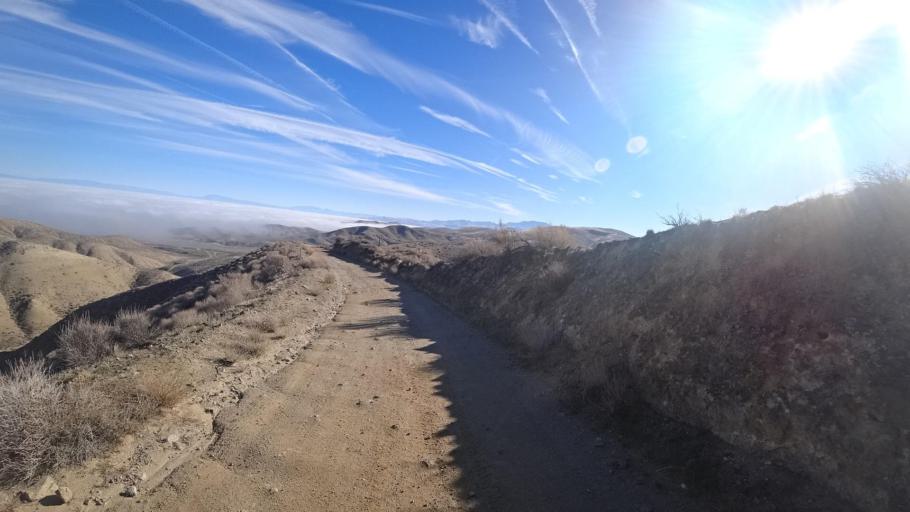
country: US
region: California
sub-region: Kern County
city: Maricopa
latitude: 35.0126
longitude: -119.4671
